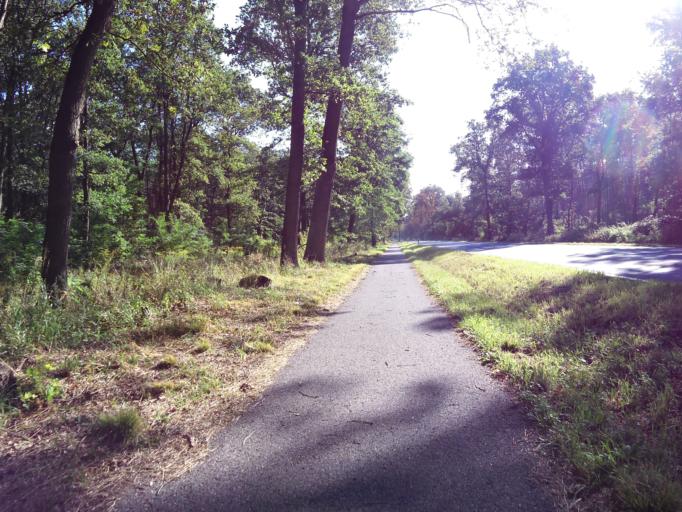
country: DE
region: Saxony-Anhalt
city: Aken
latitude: 51.8484
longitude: 12.1242
